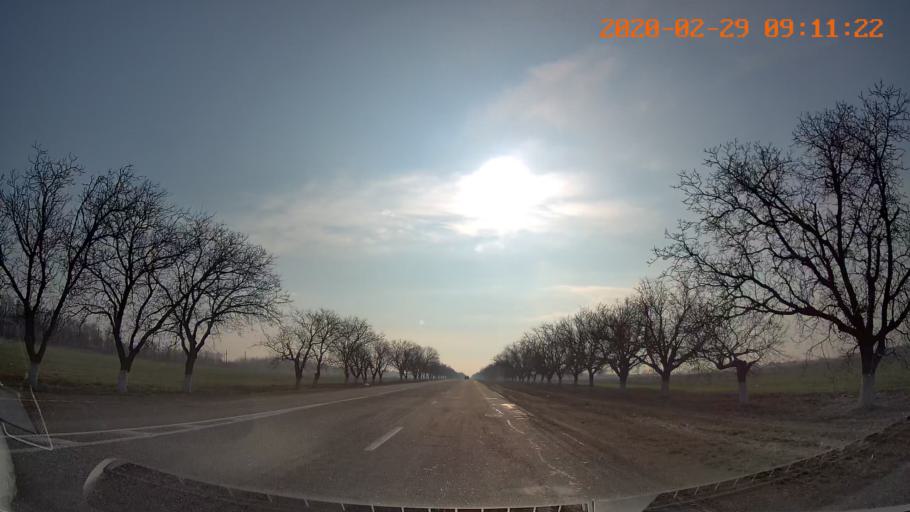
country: MD
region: Telenesti
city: Slobozia
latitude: 46.8358
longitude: 29.7985
